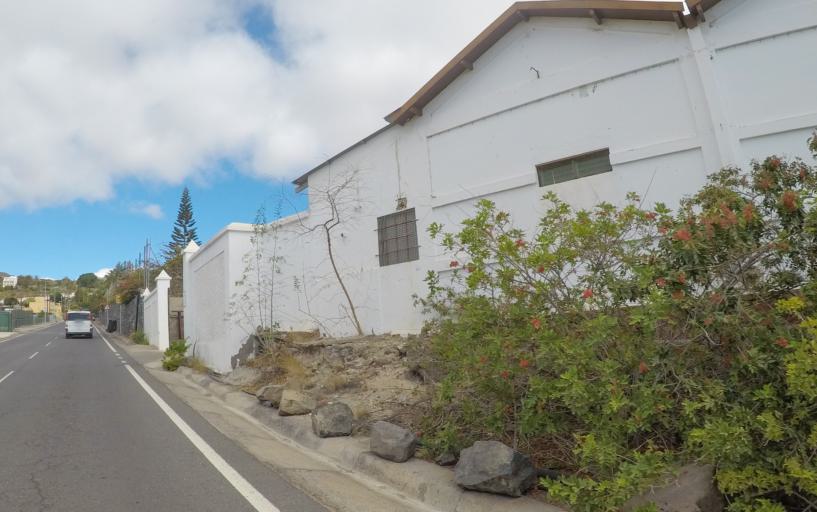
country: ES
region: Canary Islands
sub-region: Provincia de Santa Cruz de Tenerife
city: Alajero
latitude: 28.0323
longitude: -17.1907
